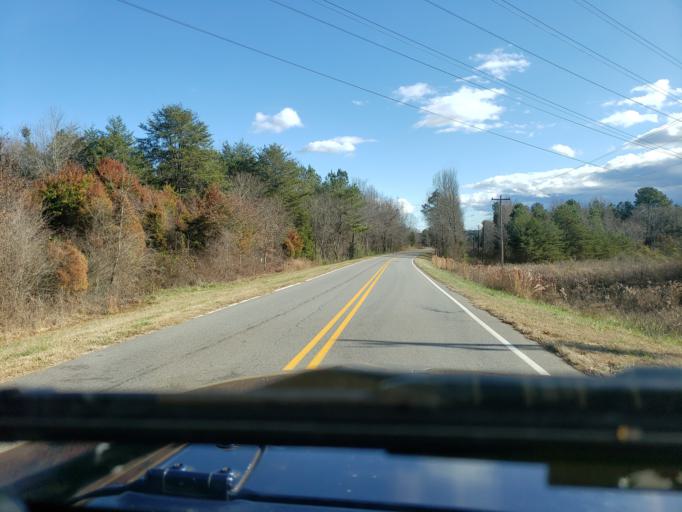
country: US
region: North Carolina
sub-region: Cleveland County
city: White Plains
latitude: 35.1715
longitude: -81.4366
